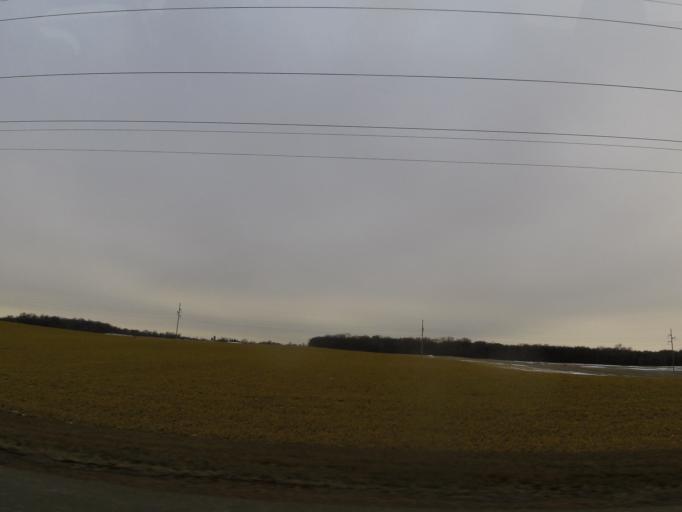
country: US
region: Minnesota
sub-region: Carver County
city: Waconia
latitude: 44.8955
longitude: -93.8185
